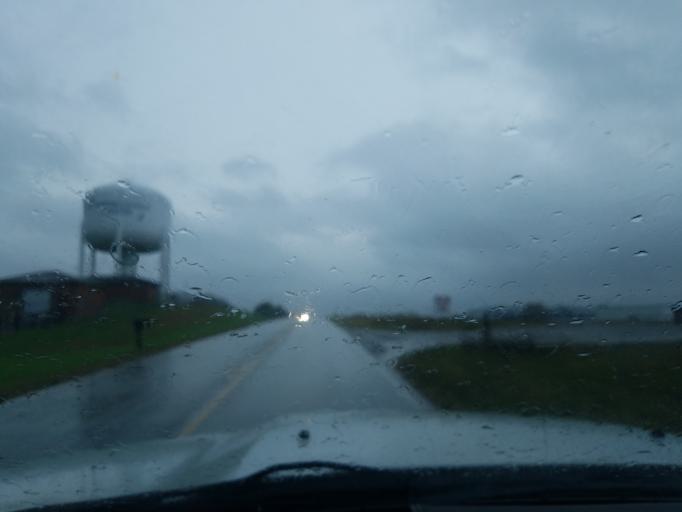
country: US
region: Kentucky
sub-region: Taylor County
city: Campbellsville
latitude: 37.3420
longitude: -85.3232
